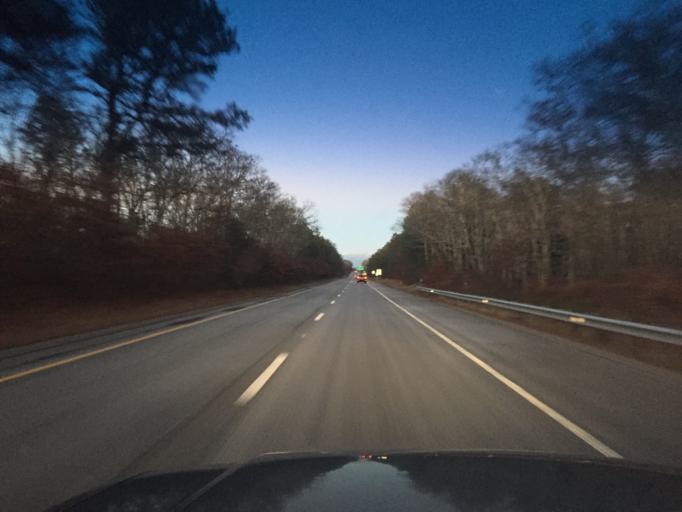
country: US
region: Massachusetts
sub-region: Barnstable County
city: West Falmouth
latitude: 41.6100
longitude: -70.6239
